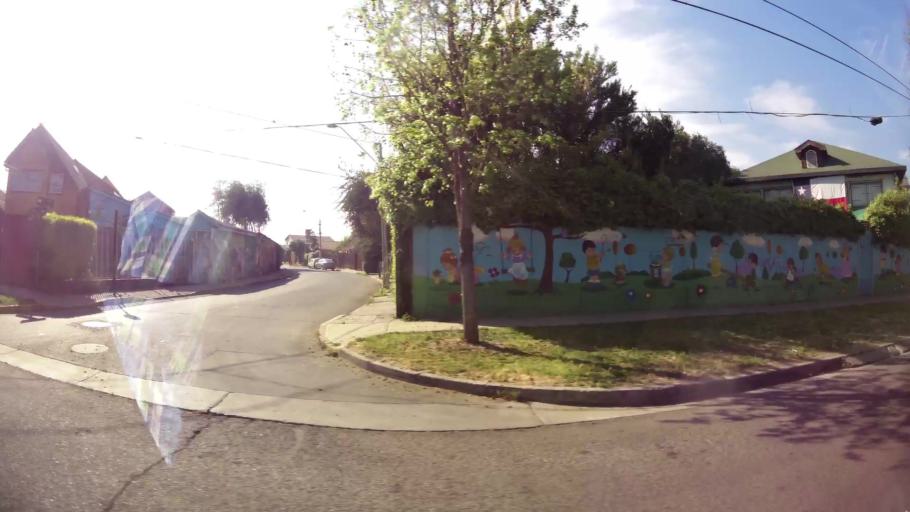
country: CL
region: Santiago Metropolitan
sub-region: Provincia de Santiago
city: Lo Prado
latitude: -33.4551
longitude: -70.7655
